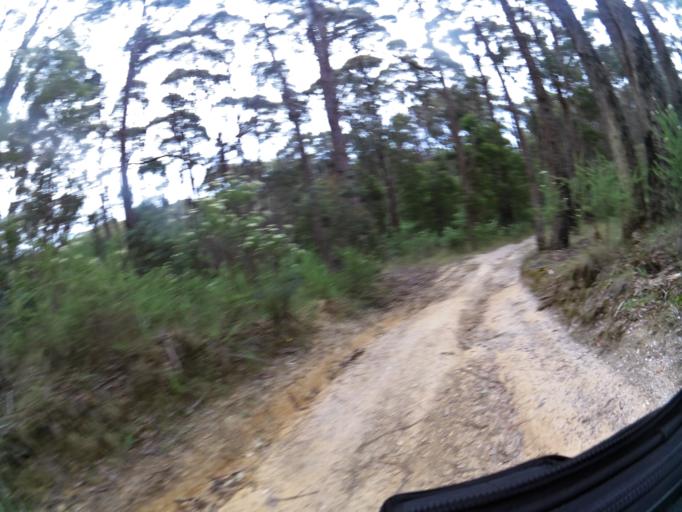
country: AU
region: Victoria
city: Brown Hill
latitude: -37.5355
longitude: 143.9015
